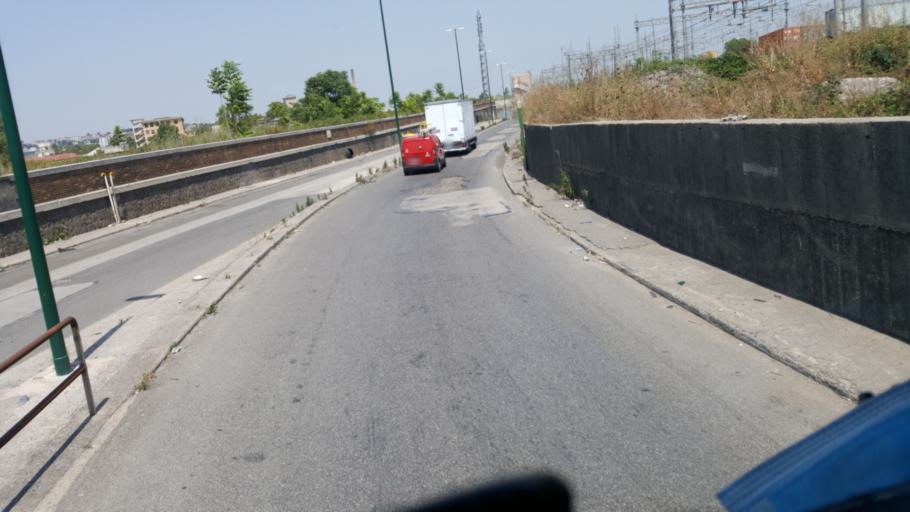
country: IT
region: Campania
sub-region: Provincia di Napoli
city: San Giorgio a Cremano
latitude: 40.8439
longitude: 14.2942
